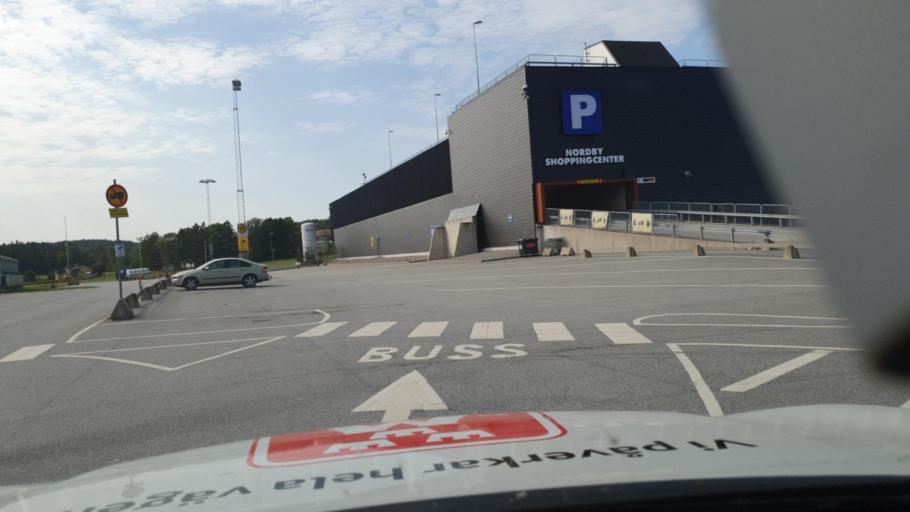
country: SE
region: Vaestra Goetaland
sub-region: Stromstads Kommun
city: Stroemstad
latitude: 59.0631
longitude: 11.2139
